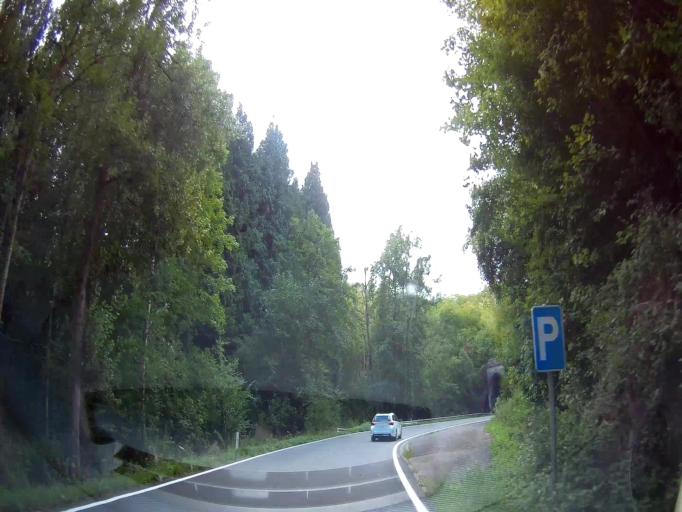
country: BE
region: Wallonia
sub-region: Province de Namur
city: Onhaye
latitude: 50.2958
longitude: 4.8152
